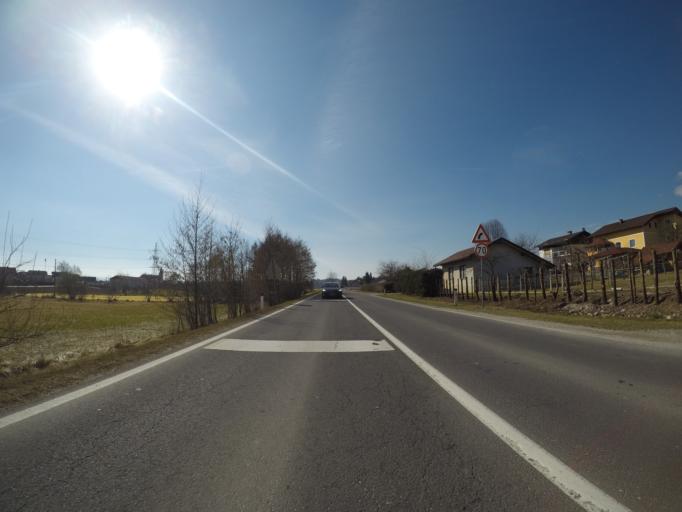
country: SI
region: Slovenska Bistrica
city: Zgornja Polskava
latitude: 46.4291
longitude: 15.6254
